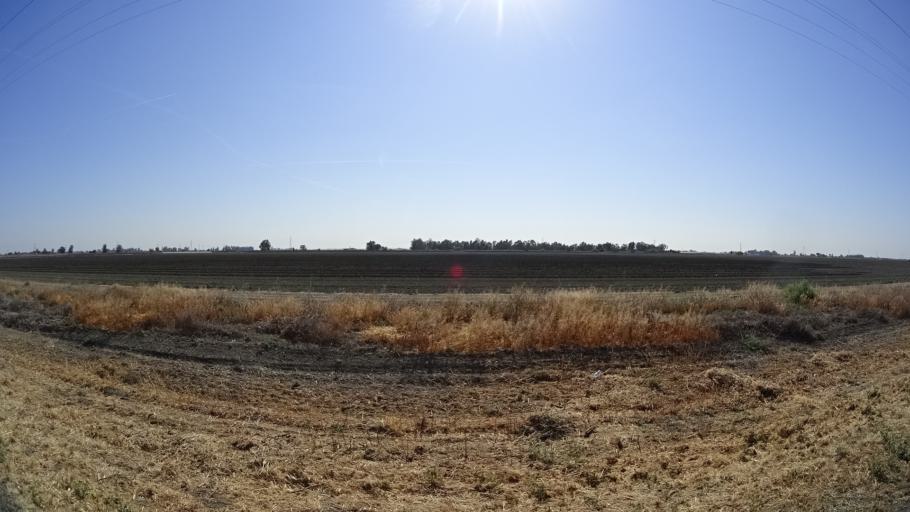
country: US
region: California
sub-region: Fresno County
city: Riverdale
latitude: 36.3542
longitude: -119.9052
